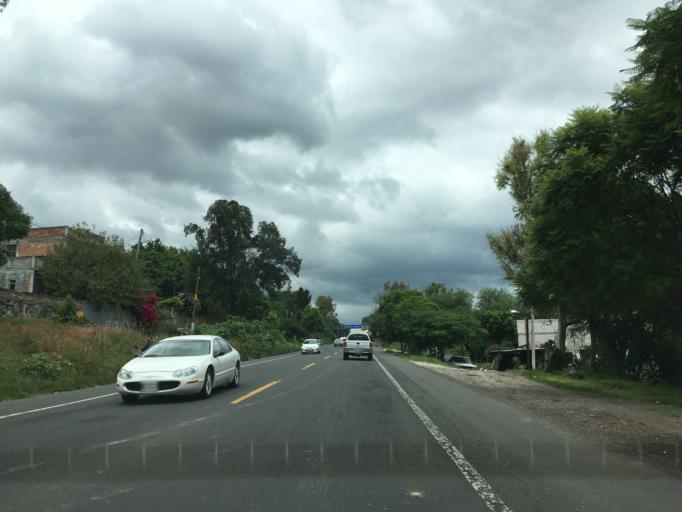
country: MX
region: Guanajuato
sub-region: Moroleon
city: Rinconadas del Bosque
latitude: 20.0951
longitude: -101.1590
